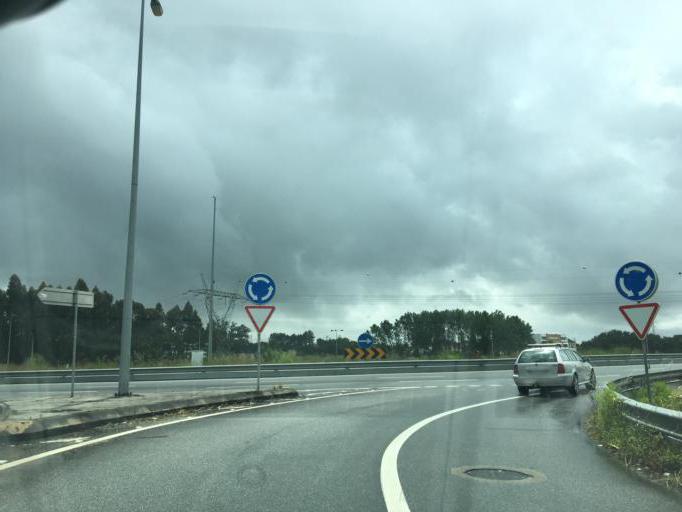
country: PT
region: Porto
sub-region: Maia
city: Nogueira
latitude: 41.2404
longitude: -8.5996
